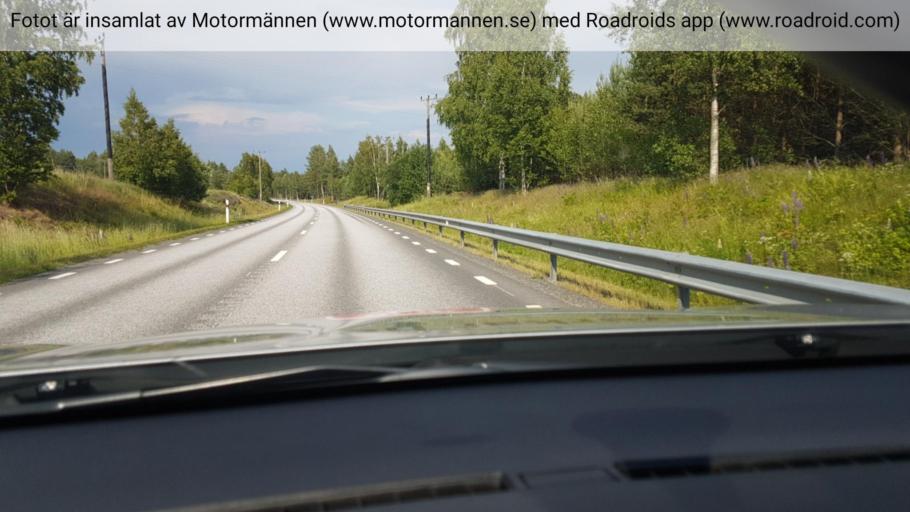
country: SE
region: Joenkoeping
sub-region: Habo Kommun
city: Habo
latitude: 58.0309
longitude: 14.1690
